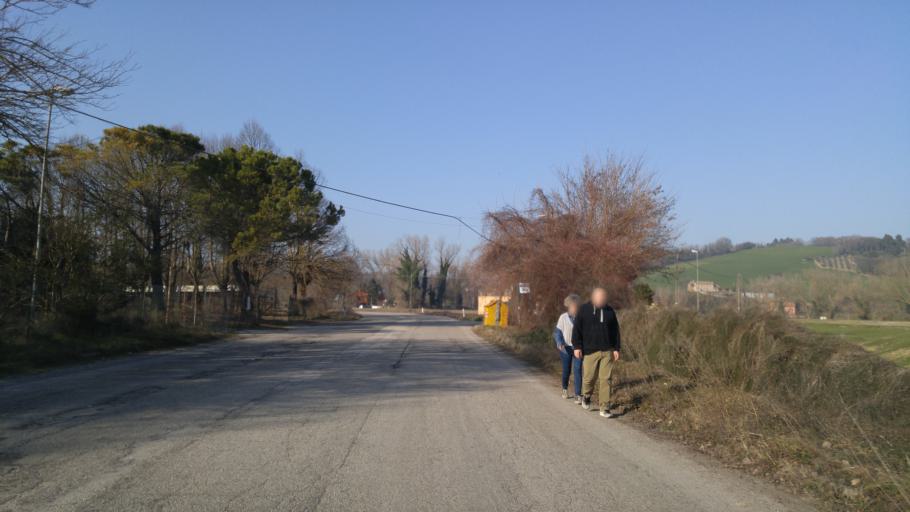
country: IT
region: The Marches
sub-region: Provincia di Pesaro e Urbino
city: Fenile
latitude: 43.8296
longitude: 12.9167
